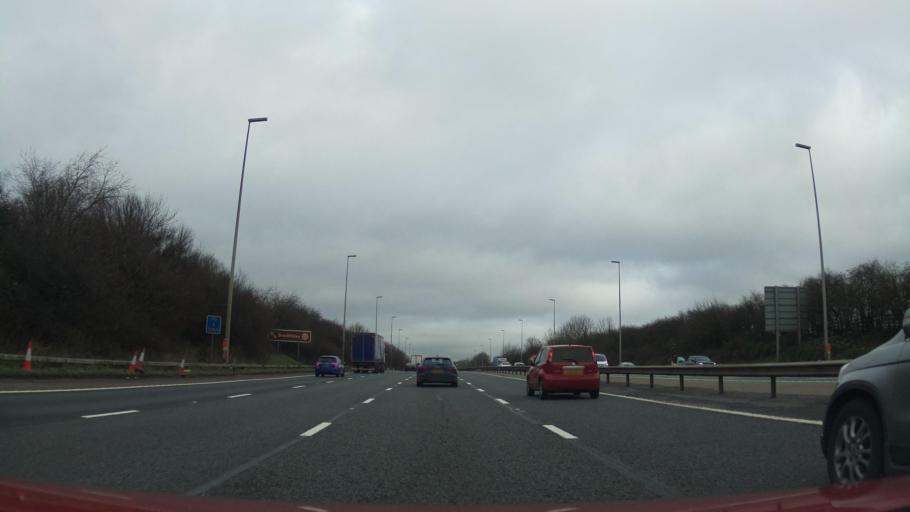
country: GB
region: England
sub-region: Lancashire
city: Clayton-le-Woods
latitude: 53.7497
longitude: -2.6453
